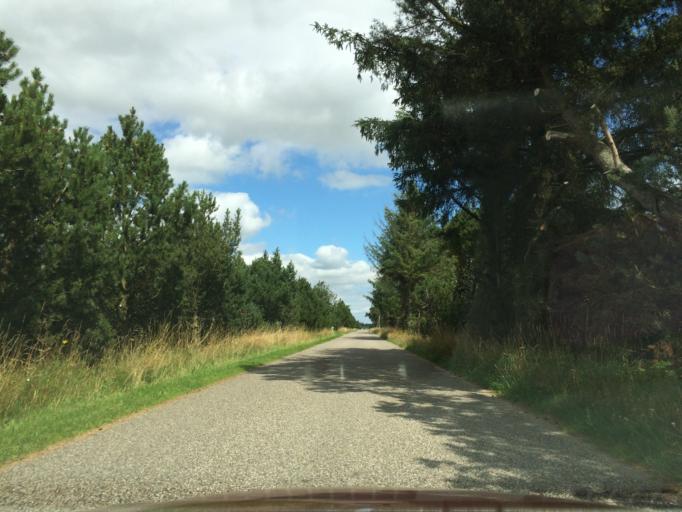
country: DK
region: Central Jutland
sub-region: Silkeborg Kommune
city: Svejbaek
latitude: 56.1898
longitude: 9.6438
